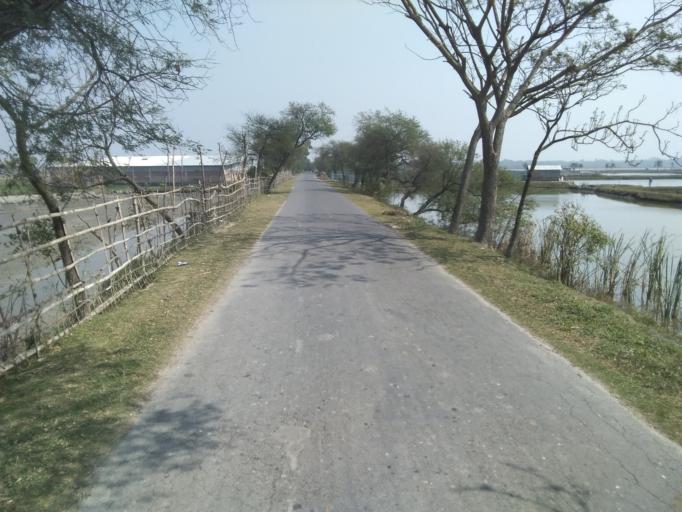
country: IN
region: West Bengal
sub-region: North 24 Parganas
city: Taki
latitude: 22.5933
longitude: 88.9777
